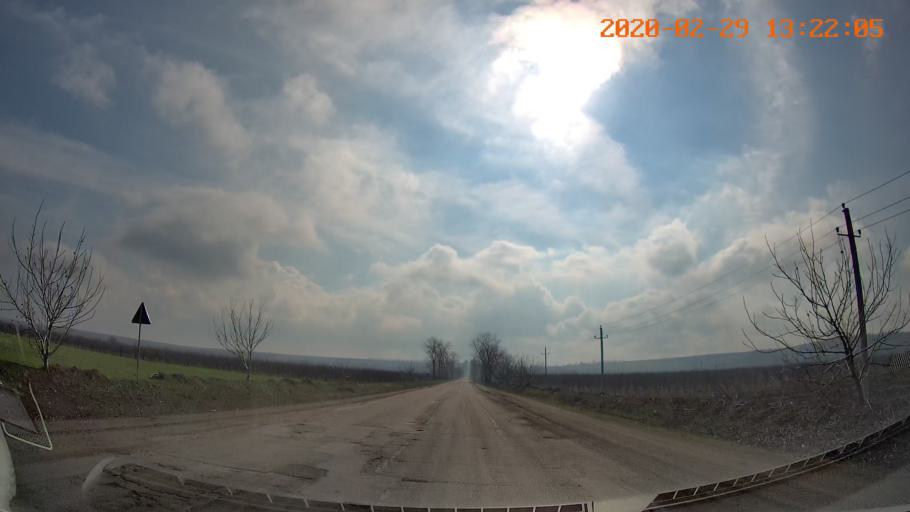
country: MD
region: Telenesti
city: Camenca
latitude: 47.9643
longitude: 28.6286
